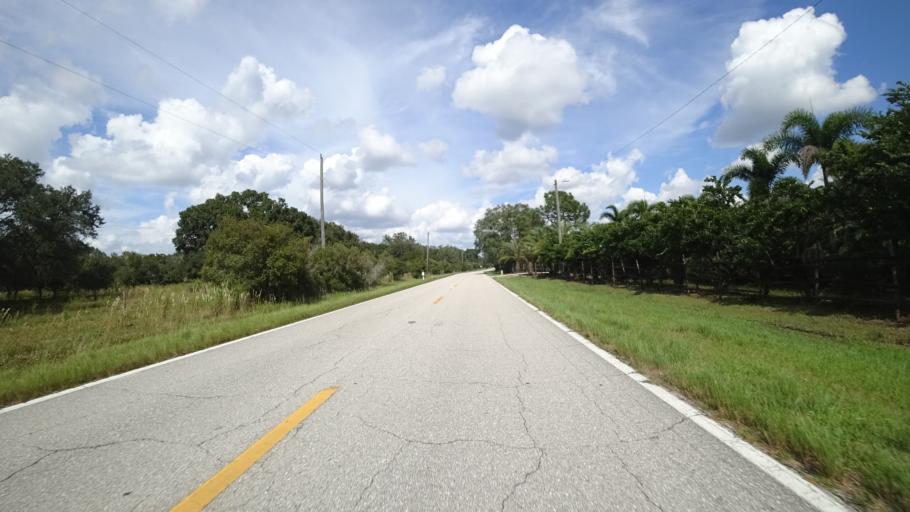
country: US
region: Florida
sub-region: Hardee County
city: Wauchula
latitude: 27.4869
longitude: -82.0777
